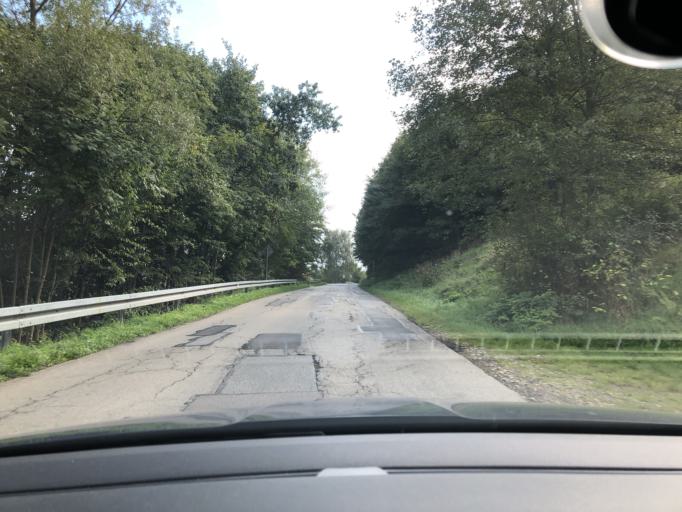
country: PL
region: Silesian Voivodeship
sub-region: Powiat zywiecki
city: Czernichow
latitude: 49.7379
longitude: 19.2070
